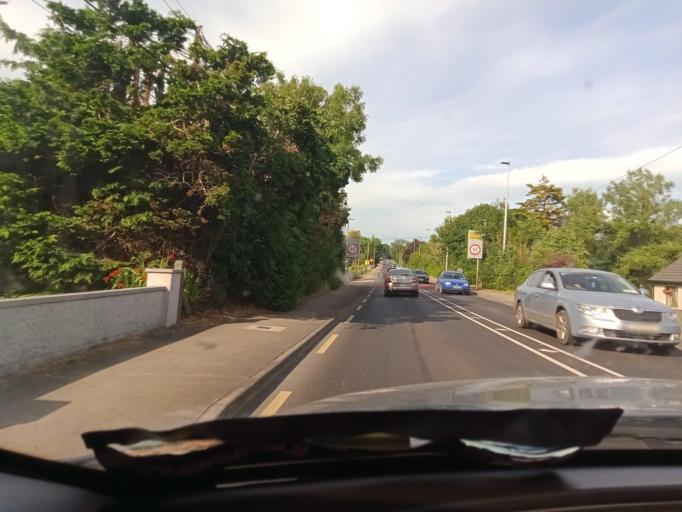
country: IE
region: Ulster
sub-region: An Cabhan
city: Cavan
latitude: 53.9356
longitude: -7.4040
